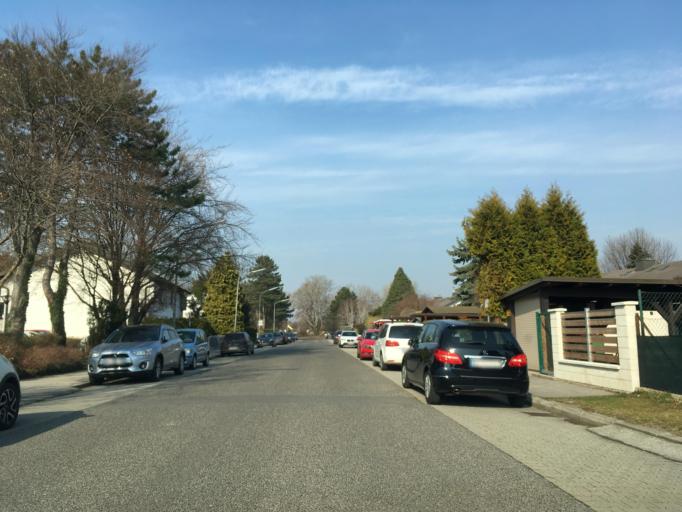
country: AT
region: Lower Austria
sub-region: Politischer Bezirk Ganserndorf
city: Gross-Enzersdorf
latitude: 48.2097
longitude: 16.4754
